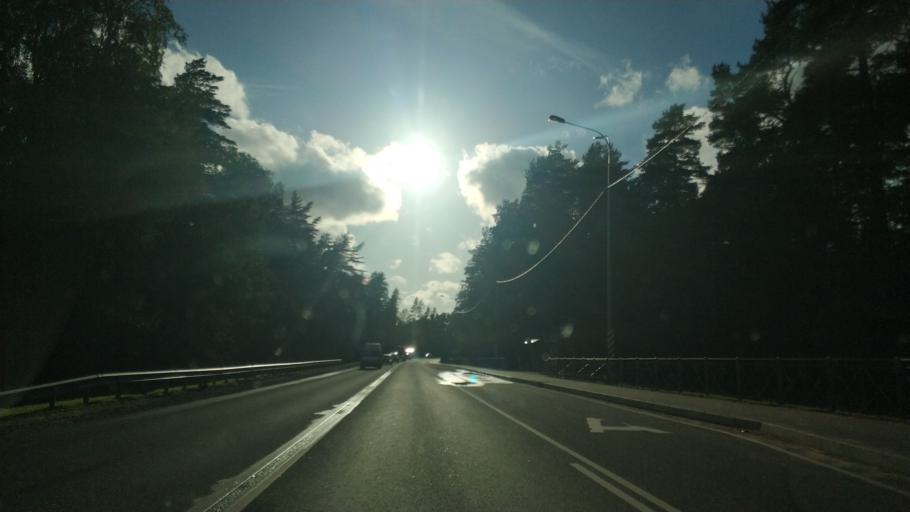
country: RU
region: Leningrad
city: Sapernoye
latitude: 60.7131
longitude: 30.0330
